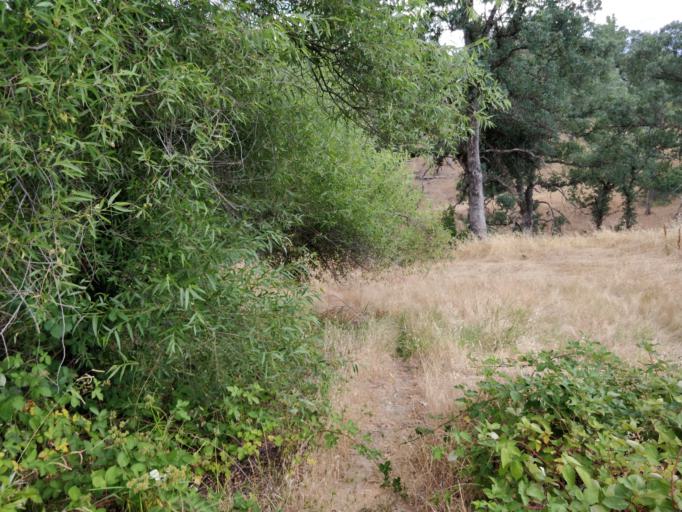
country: US
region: California
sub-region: Shasta County
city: Redding
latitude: 40.6119
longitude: -122.3854
